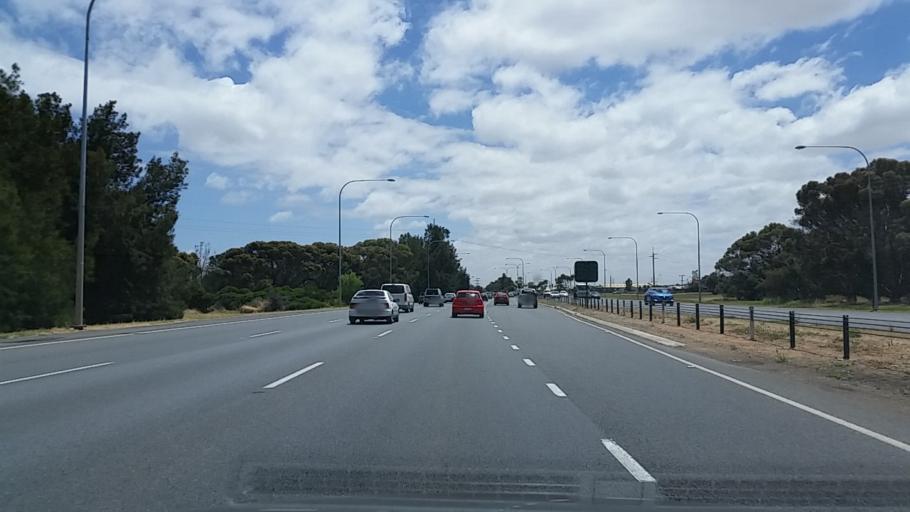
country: AU
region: South Australia
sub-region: Salisbury
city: Salisbury
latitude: -34.7970
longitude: 138.5963
